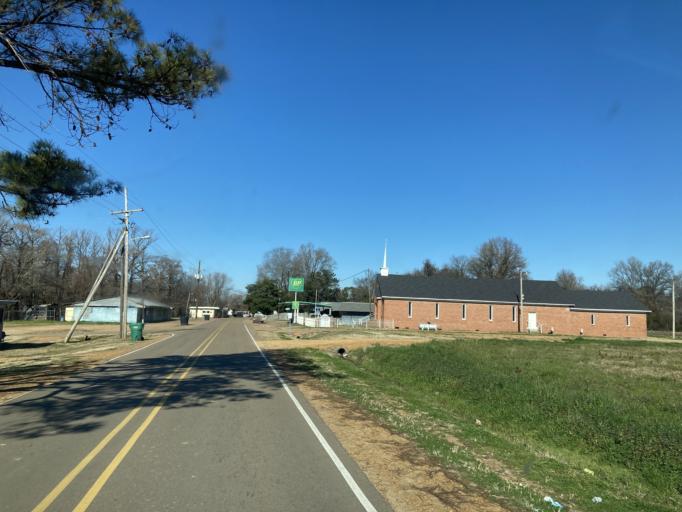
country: US
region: Mississippi
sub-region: Yazoo County
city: Yazoo City
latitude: 32.9772
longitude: -90.5905
